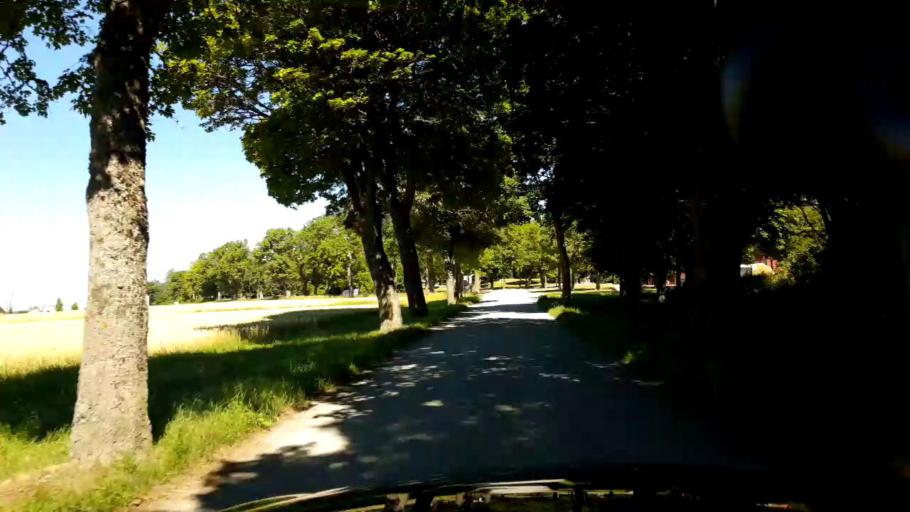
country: SE
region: Stockholm
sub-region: Sigtuna Kommun
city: Sigtuna
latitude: 59.6048
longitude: 17.6458
